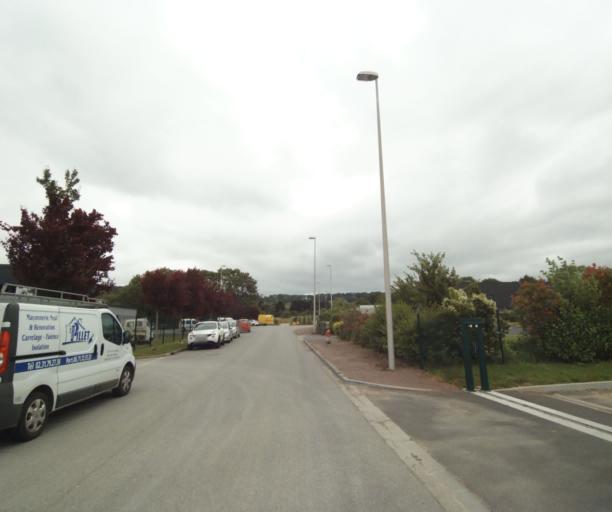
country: FR
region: Lower Normandy
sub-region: Departement du Calvados
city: Dives-sur-Mer
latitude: 49.2748
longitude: -0.0923
